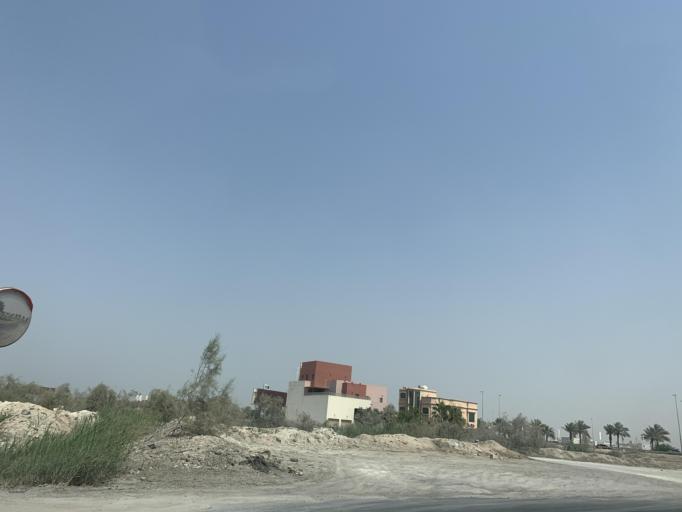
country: BH
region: Northern
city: Madinat `Isa
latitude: 26.1944
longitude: 50.5169
